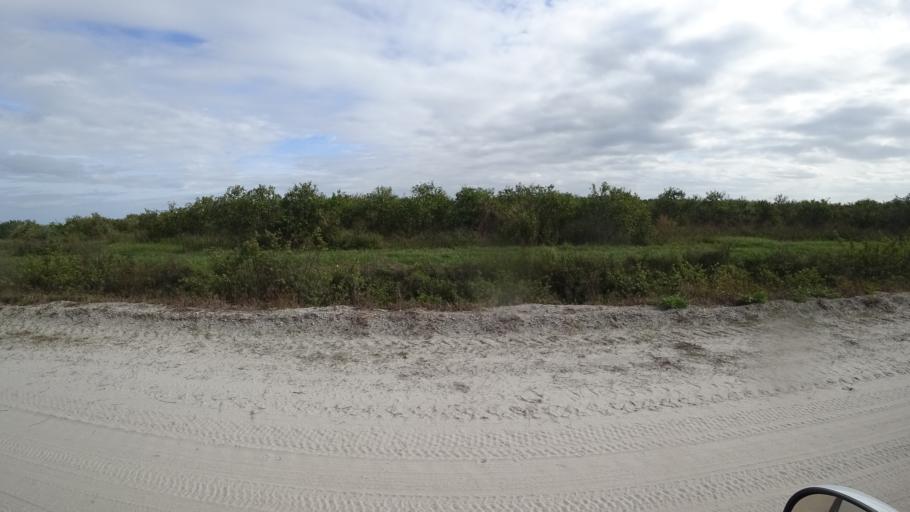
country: US
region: Florida
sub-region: Hillsborough County
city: Wimauma
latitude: 27.5745
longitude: -82.3129
